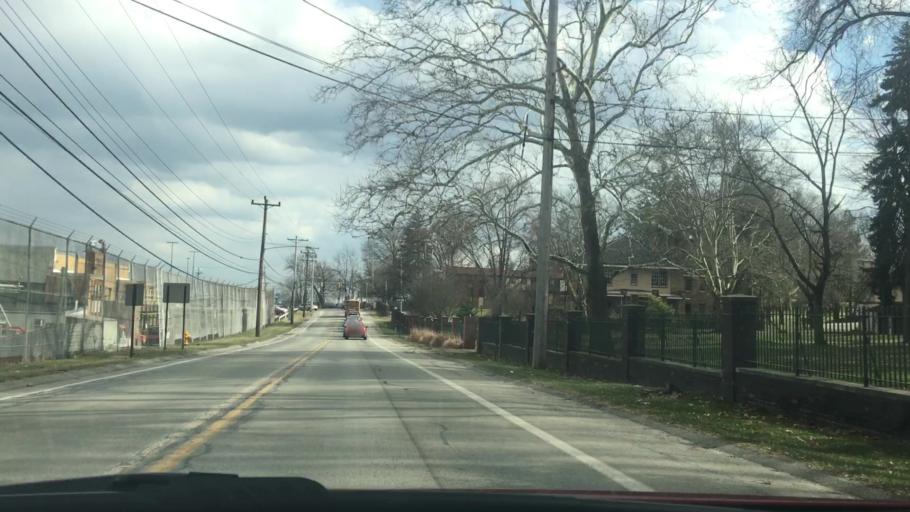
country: US
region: Pennsylvania
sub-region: Allegheny County
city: Dravosburg
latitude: 40.3580
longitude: -79.9019
